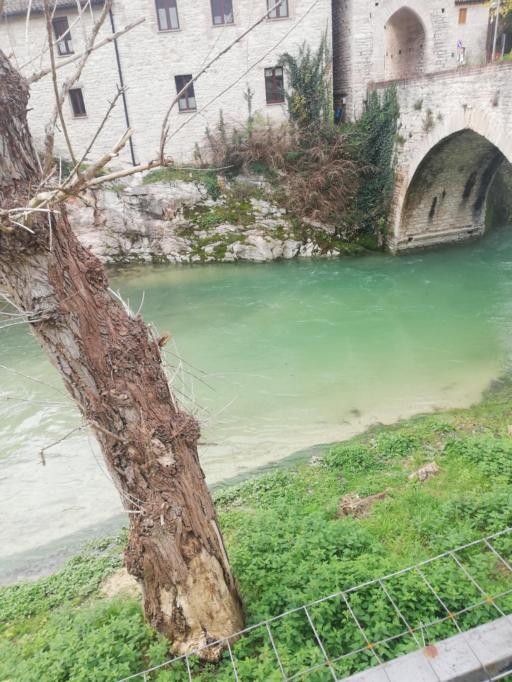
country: IT
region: The Marches
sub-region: Provincia di Ancona
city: Genga
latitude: 43.4026
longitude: 12.9713
